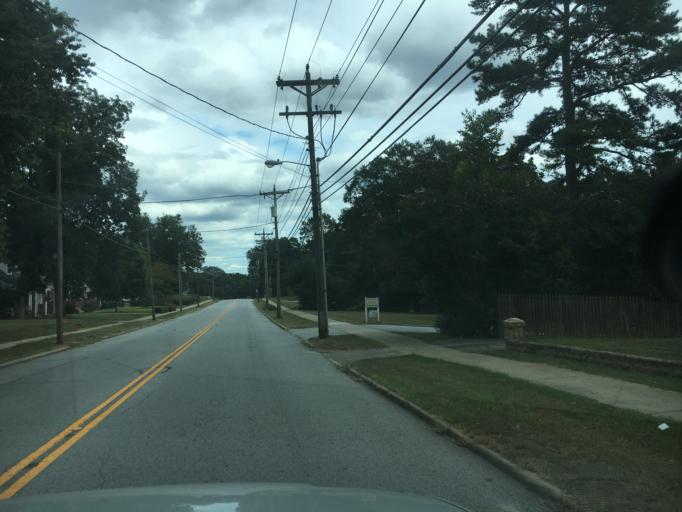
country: US
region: South Carolina
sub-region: Laurens County
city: Laurens
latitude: 34.4948
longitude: -82.0269
